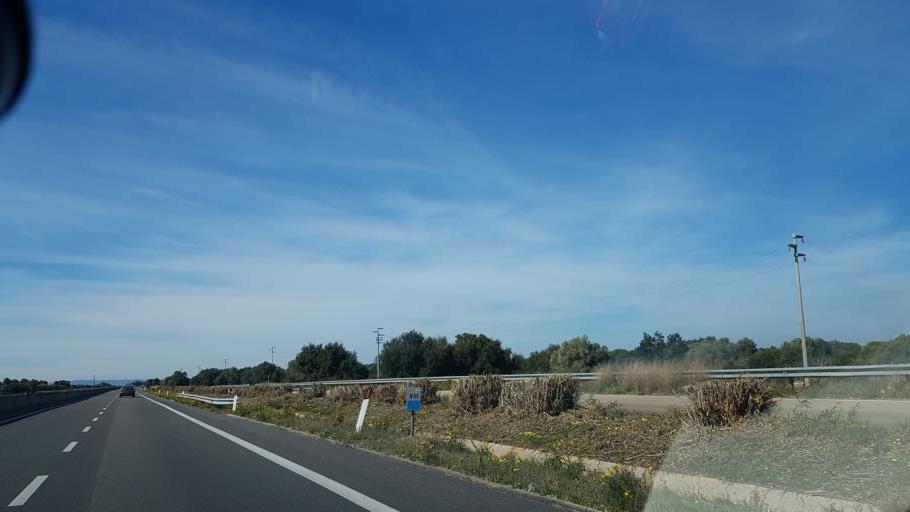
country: IT
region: Apulia
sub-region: Provincia di Brindisi
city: Carovigno
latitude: 40.7610
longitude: 17.6560
